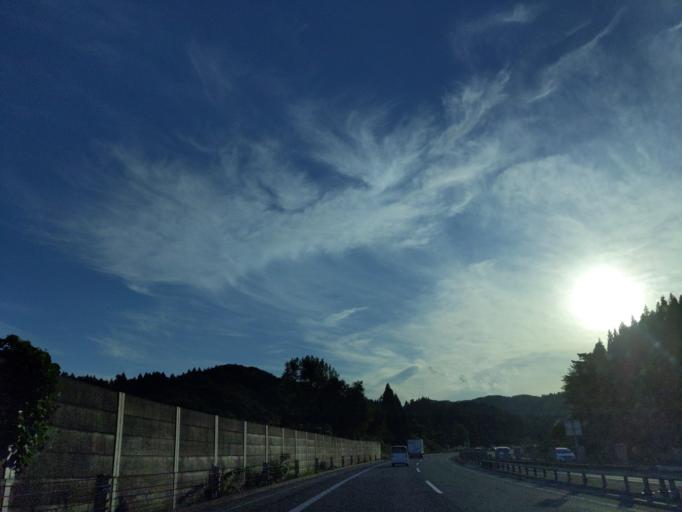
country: JP
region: Niigata
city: Nagaoka
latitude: 37.4355
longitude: 138.7245
